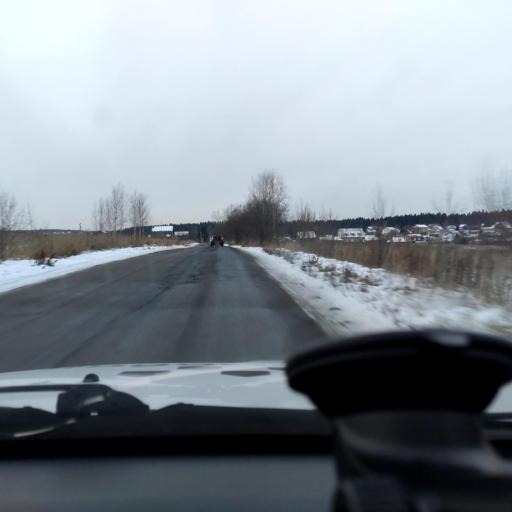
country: RU
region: Perm
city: Ferma
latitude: 57.9325
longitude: 56.3277
